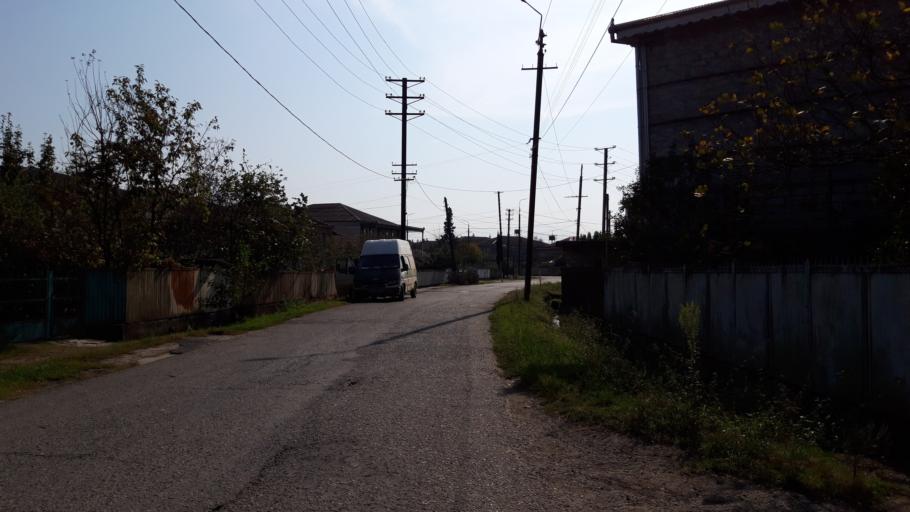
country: GE
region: Imereti
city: Samtredia
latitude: 42.1629
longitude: 42.3335
